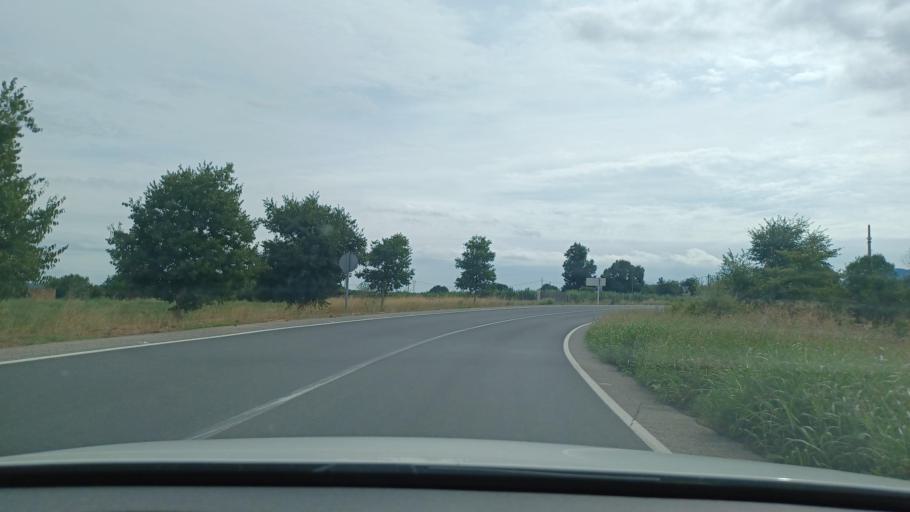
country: ES
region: Catalonia
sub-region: Provincia de Tarragona
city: Santa Barbara
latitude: 40.7225
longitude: 0.5036
